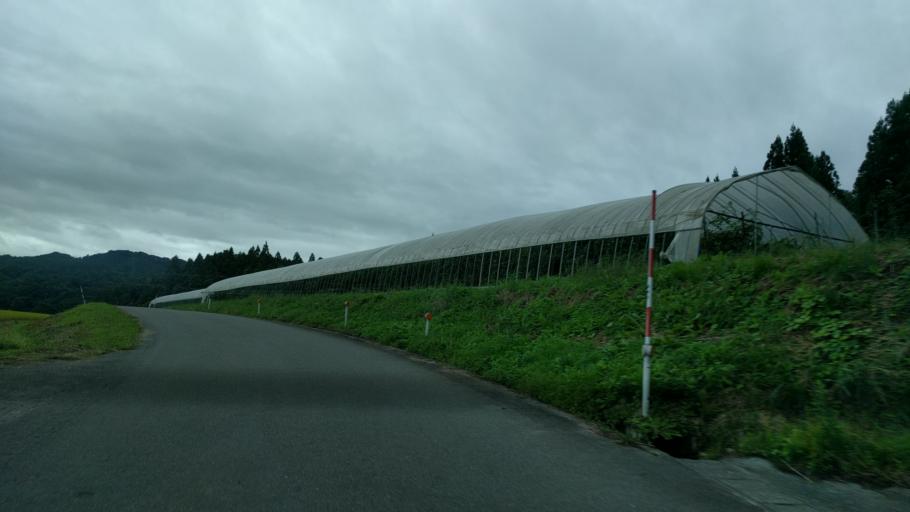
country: JP
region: Fukushima
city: Kitakata
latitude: 37.5406
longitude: 139.7345
